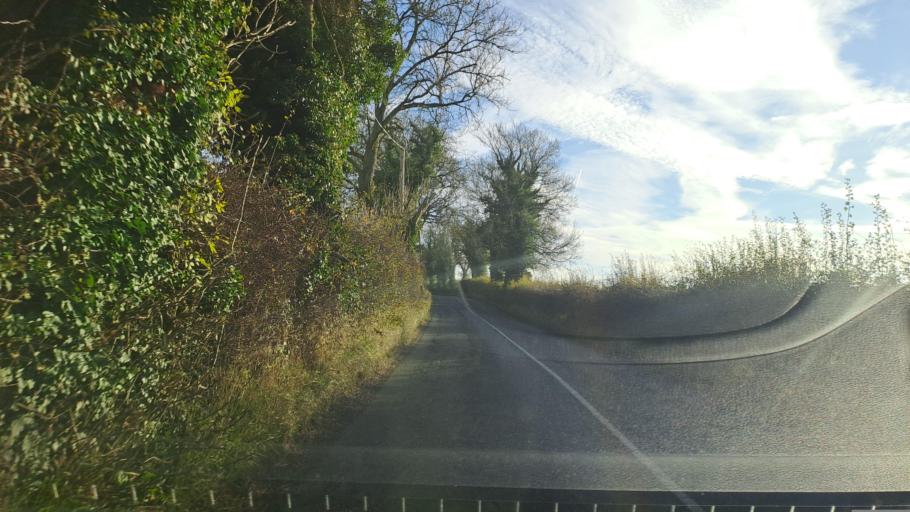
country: IE
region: Leinster
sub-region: Lu
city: Ardee
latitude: 53.8560
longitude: -6.6669
